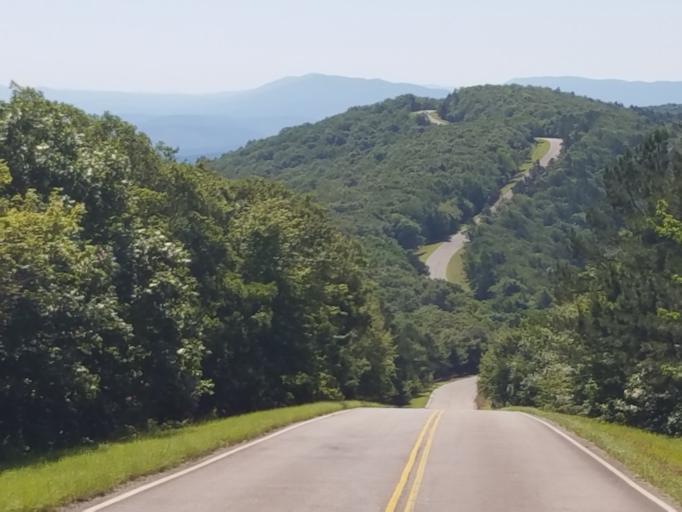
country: US
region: Oklahoma
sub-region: Le Flore County
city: Wister
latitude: 34.7483
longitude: -94.7886
